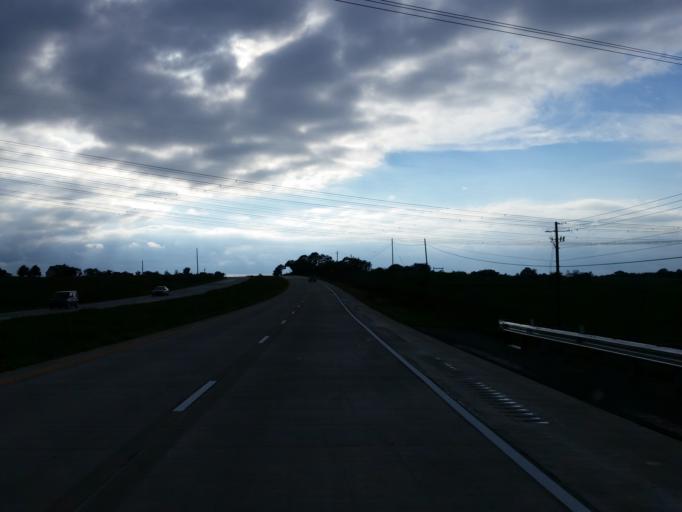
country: US
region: Georgia
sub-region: Bartow County
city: Euharlee
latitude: 34.1082
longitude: -84.9062
